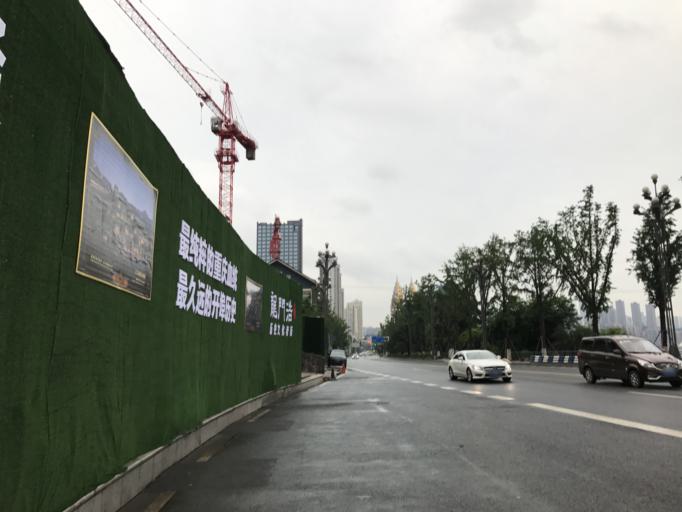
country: CN
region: Chongqing Shi
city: Nanping
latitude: 29.5598
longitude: 106.5907
